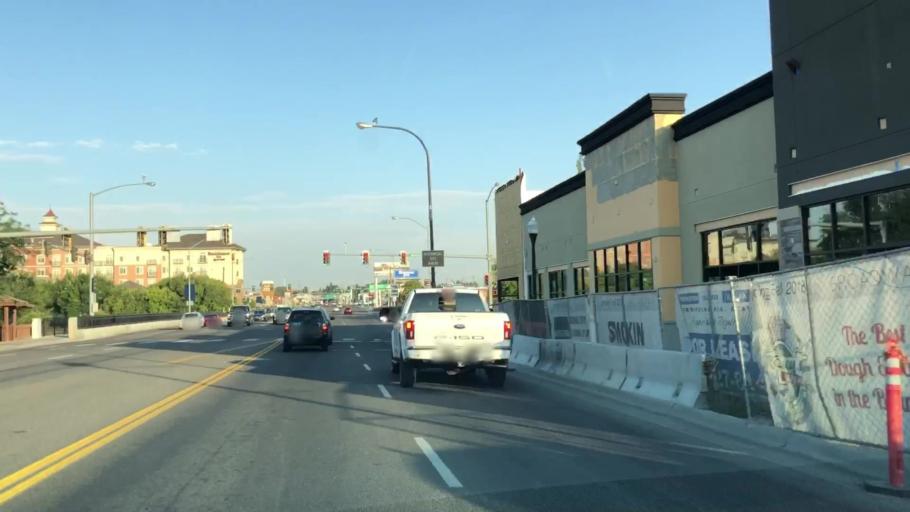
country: US
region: Idaho
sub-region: Bonneville County
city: Idaho Falls
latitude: 43.4925
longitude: -112.0431
